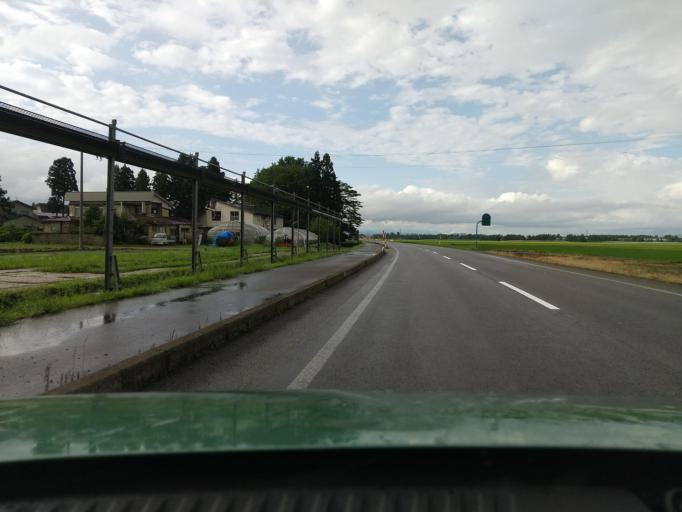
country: JP
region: Akita
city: Omagari
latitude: 39.3872
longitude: 140.4735
